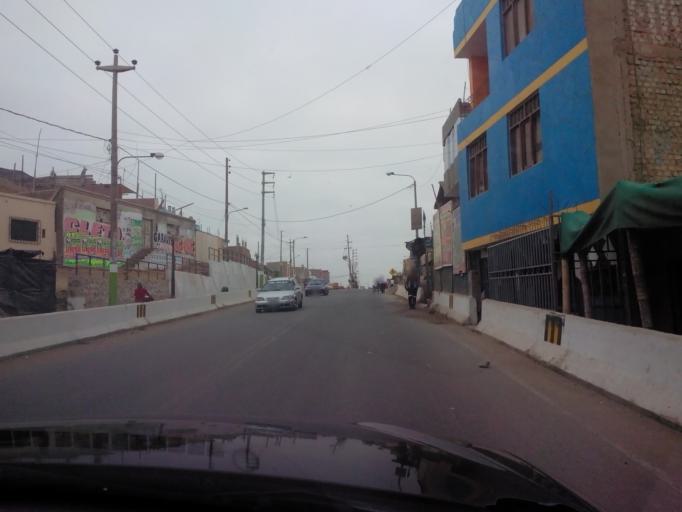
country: PE
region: Ica
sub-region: Provincia de Pisco
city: San Clemente
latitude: -13.6827
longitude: -76.1581
